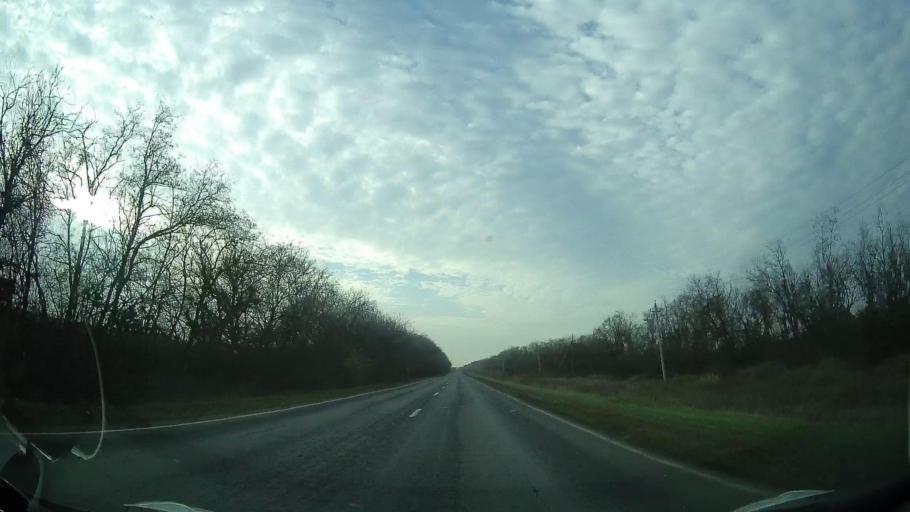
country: RU
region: Rostov
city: Bagayevskaya
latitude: 47.0928
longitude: 40.3640
